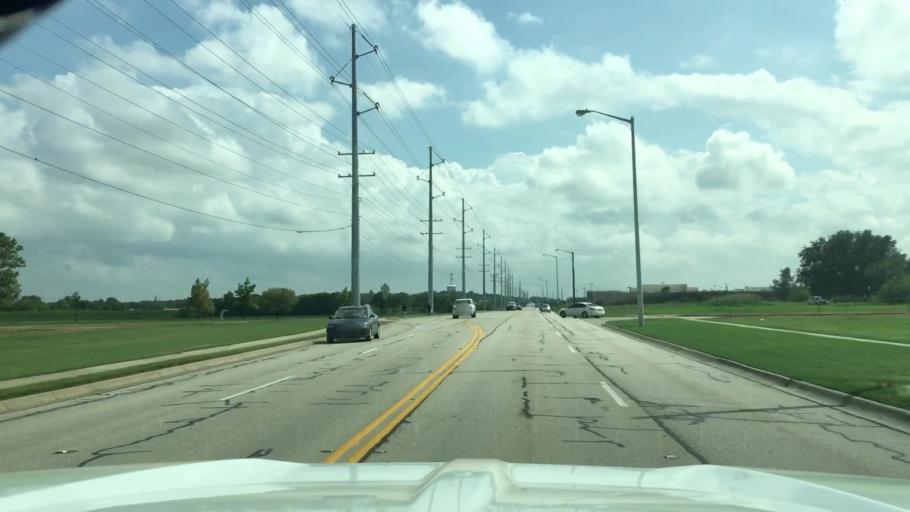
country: US
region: Texas
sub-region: Denton County
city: Denton
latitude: 33.2373
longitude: -97.1608
